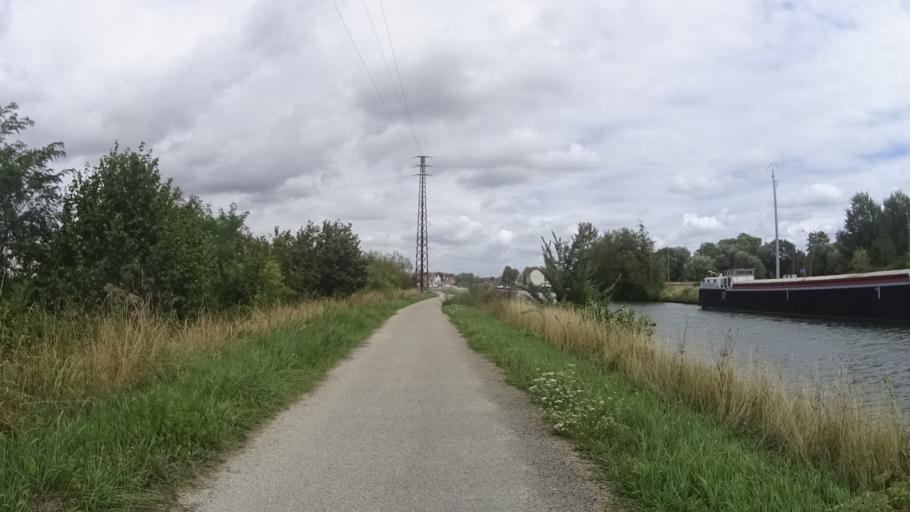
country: FR
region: Picardie
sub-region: Departement de l'Aisne
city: Chauny
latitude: 49.6044
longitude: 3.2163
